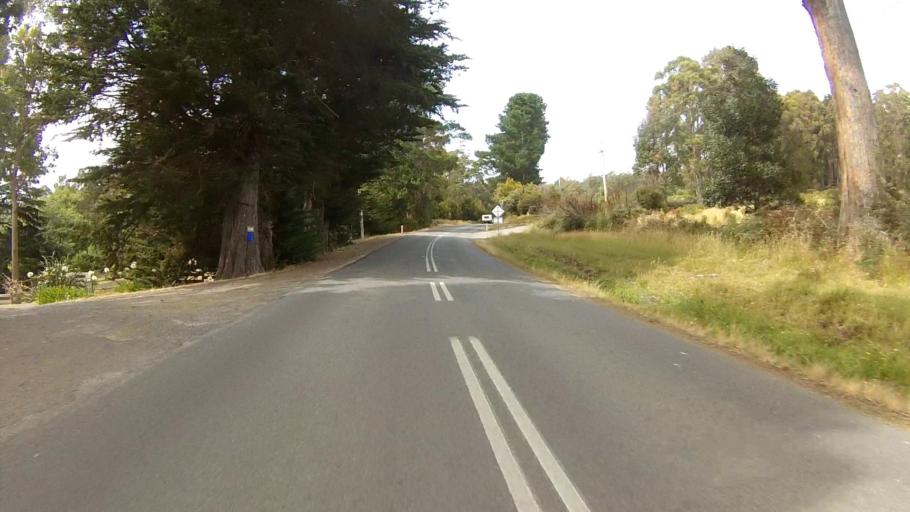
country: AU
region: Tasmania
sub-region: Kingborough
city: Kettering
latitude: -43.1888
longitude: 147.2450
